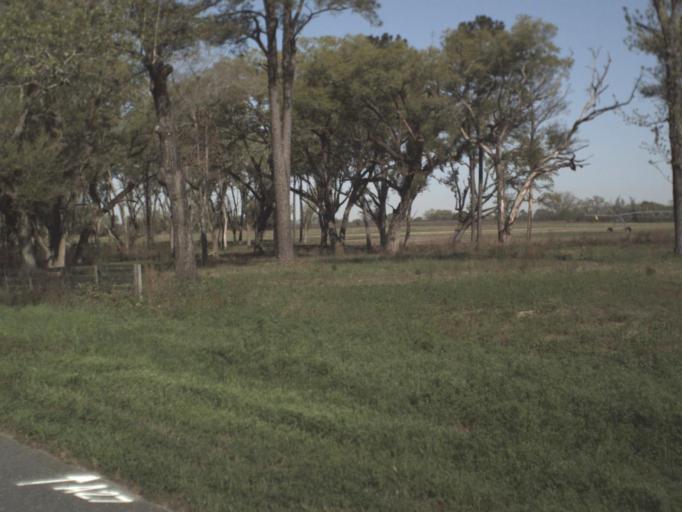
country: US
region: Florida
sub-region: Jackson County
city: Malone
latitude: 30.9590
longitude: -85.1857
